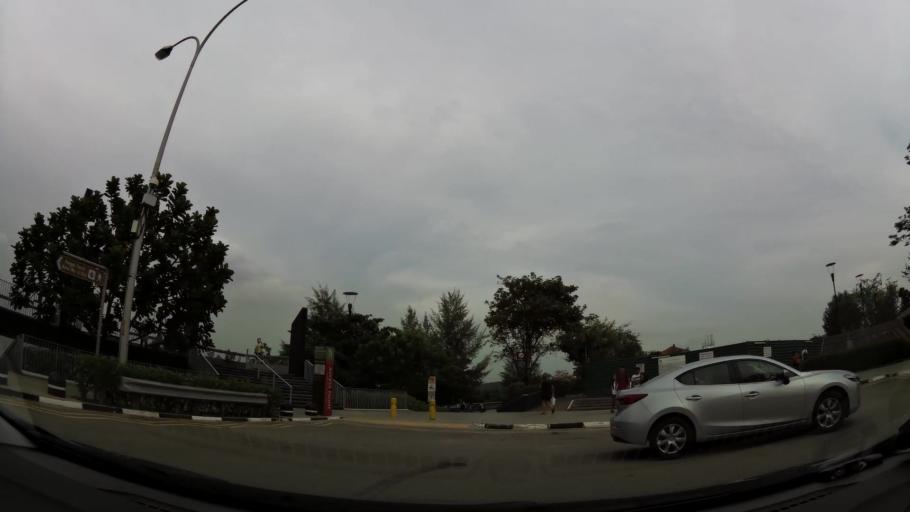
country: MY
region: Johor
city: Kampung Pasir Gudang Baru
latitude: 1.4213
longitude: 103.9106
